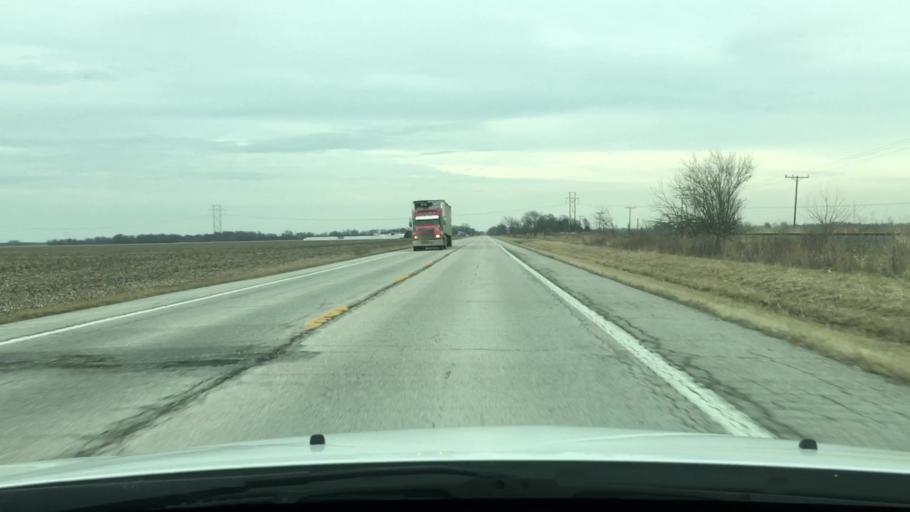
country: US
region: Missouri
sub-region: Audrain County
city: Vandalia
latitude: 39.2880
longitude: -91.5386
